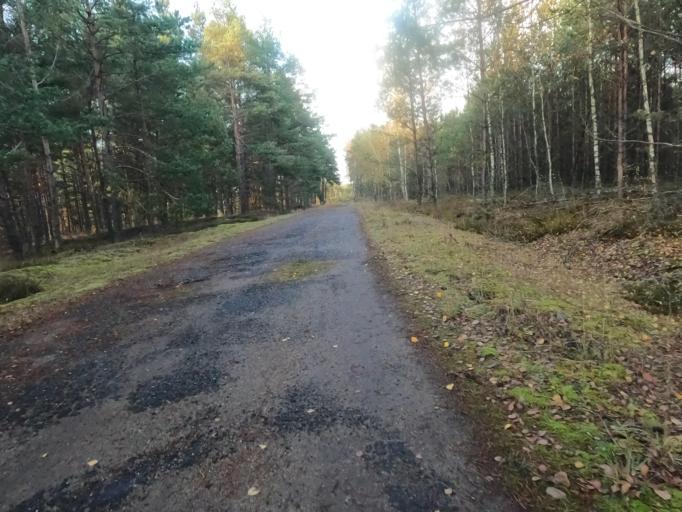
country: PL
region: West Pomeranian Voivodeship
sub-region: Powiat szczecinecki
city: Borne Sulinowo
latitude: 53.5518
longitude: 16.5219
